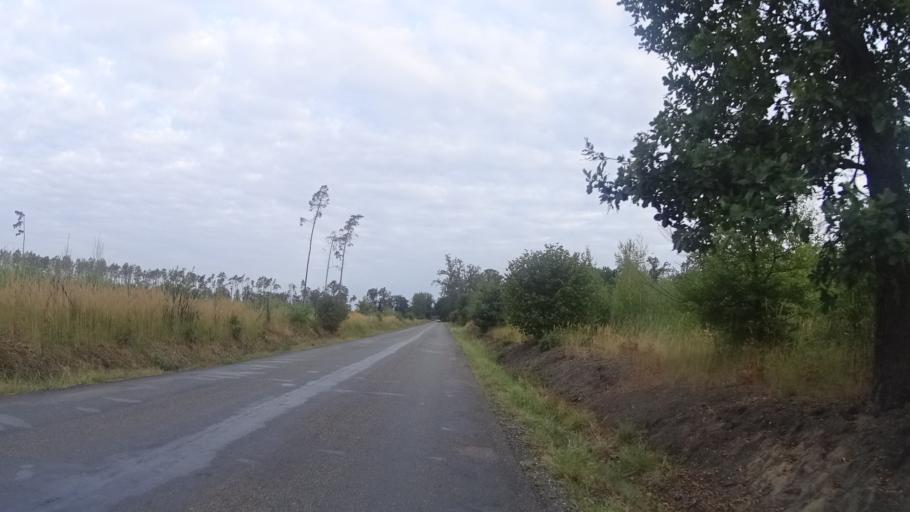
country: CZ
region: Kralovehradecky
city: Cernilov
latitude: 50.2066
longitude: 15.9243
